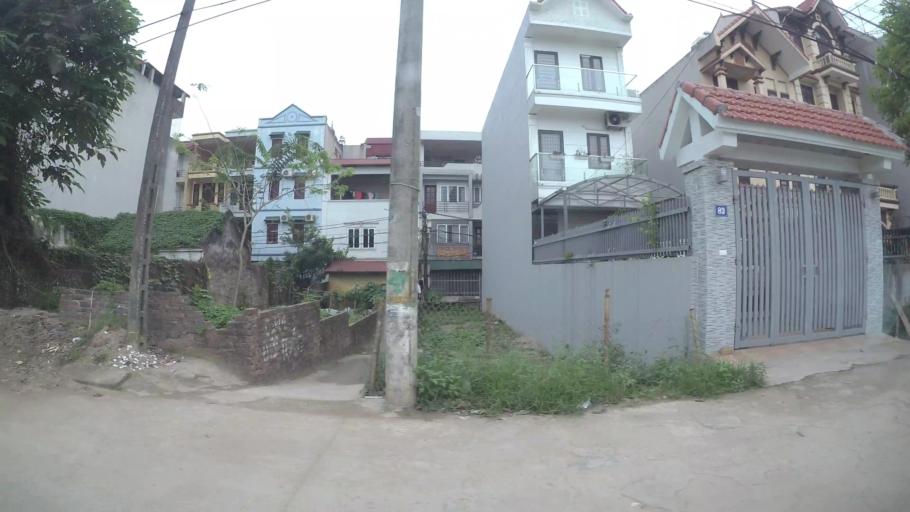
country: VN
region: Ha Noi
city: Tay Ho
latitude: 21.0773
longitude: 105.8245
